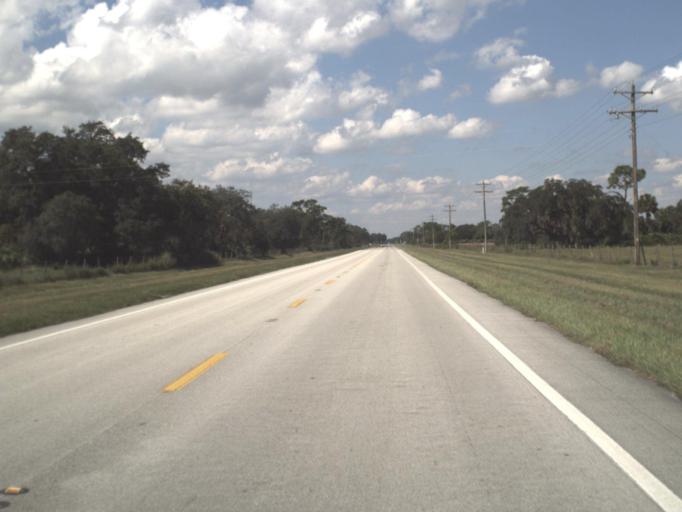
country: US
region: Florida
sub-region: Okeechobee County
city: Okeechobee
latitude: 27.3847
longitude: -81.0000
